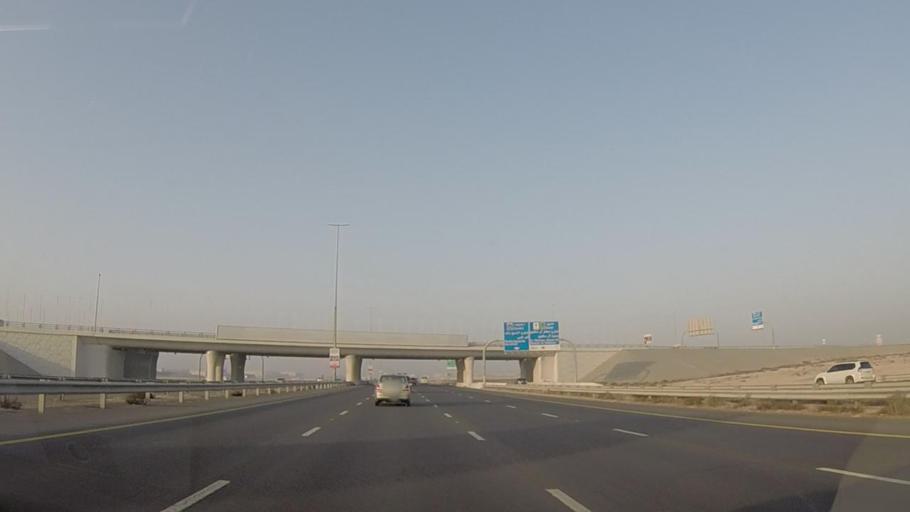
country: AE
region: Dubai
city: Dubai
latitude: 24.9444
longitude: 55.0545
